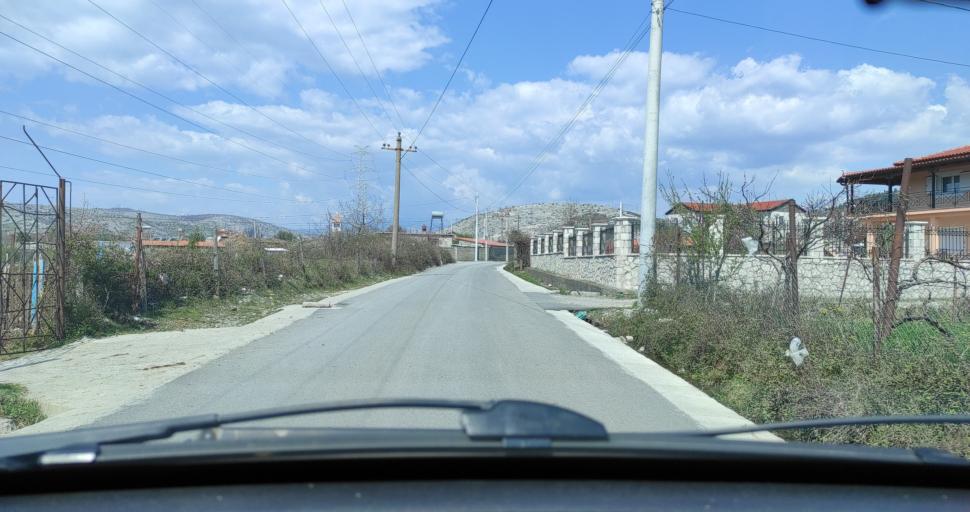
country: AL
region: Shkoder
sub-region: Rrethi i Shkodres
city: Vau i Dejes
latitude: 42.0030
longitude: 19.6420
